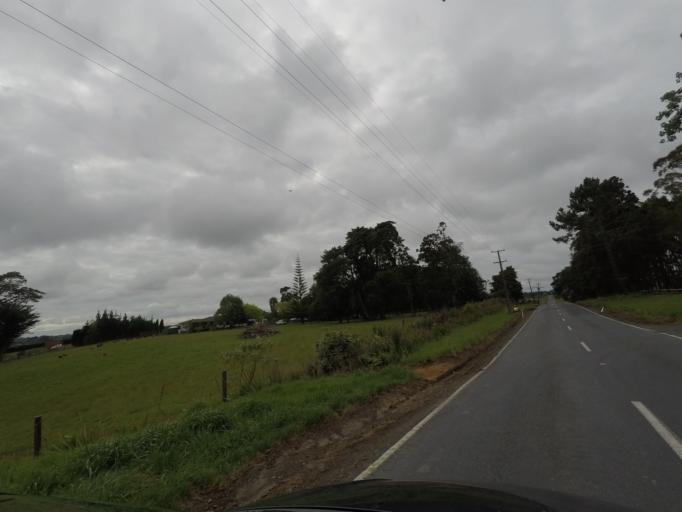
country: NZ
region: Auckland
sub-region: Auckland
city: Rosebank
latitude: -36.8044
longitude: 174.5748
